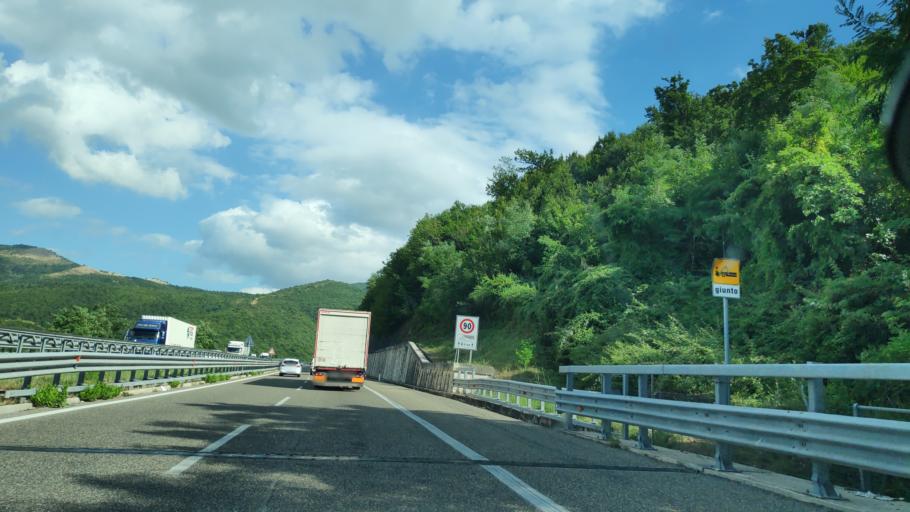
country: IT
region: Campania
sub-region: Provincia di Salerno
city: Pertosa
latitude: 40.5329
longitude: 15.4249
